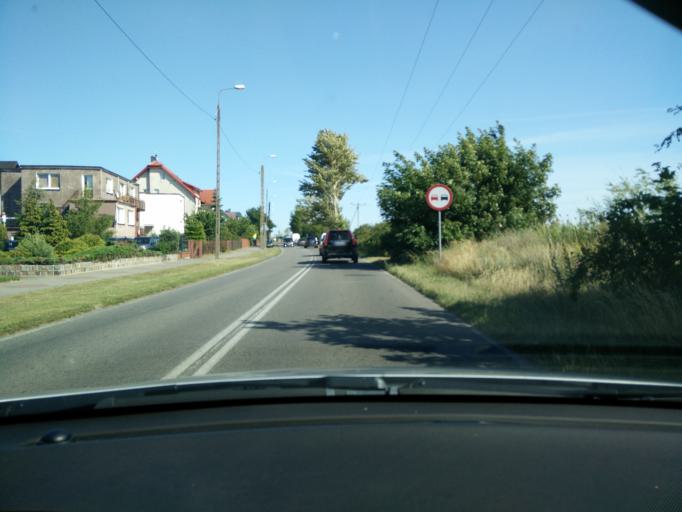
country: PL
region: Pomeranian Voivodeship
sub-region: Powiat pucki
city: Jastarnia
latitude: 54.7297
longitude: 18.5931
